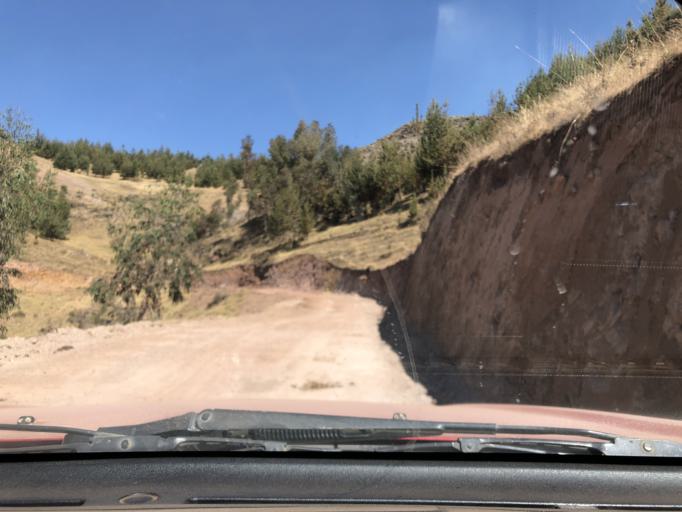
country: PE
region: Ayacucho
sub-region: Provincia de La Mar
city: Chilcas
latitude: -13.1816
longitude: -73.8451
